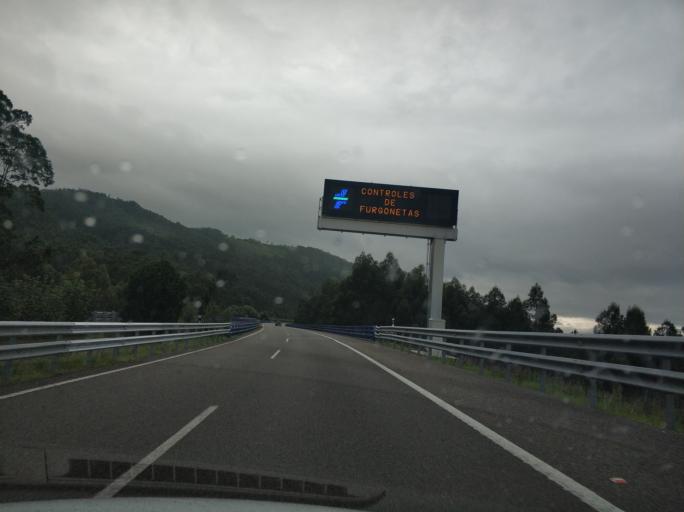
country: ES
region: Galicia
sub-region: Provincia de Lugo
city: Ribadeo
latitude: 43.5355
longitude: -7.1328
